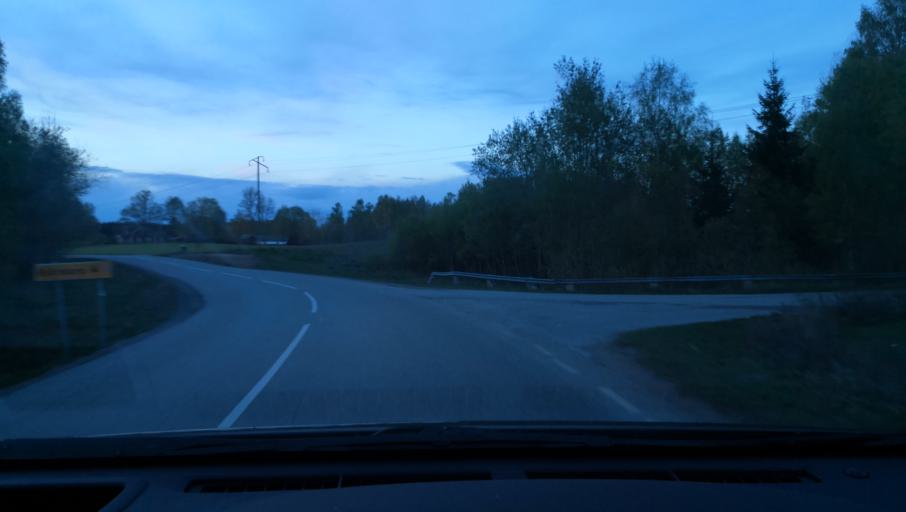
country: SE
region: OErebro
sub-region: Askersunds Kommun
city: Askersund
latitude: 58.9992
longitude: 14.8974
